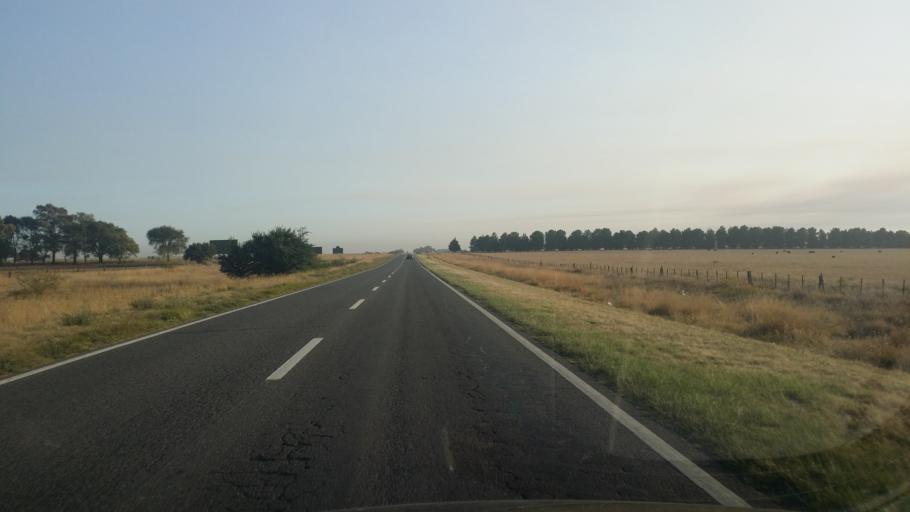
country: AR
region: La Pampa
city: Santa Rosa
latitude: -36.4672
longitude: -64.2800
